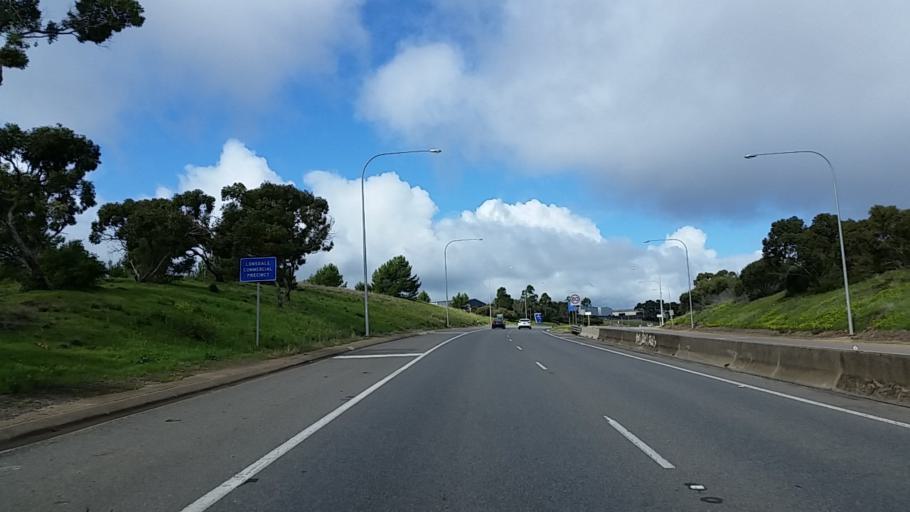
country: AU
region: South Australia
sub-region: Onkaparinga
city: Reynella
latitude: -35.0996
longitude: 138.4987
